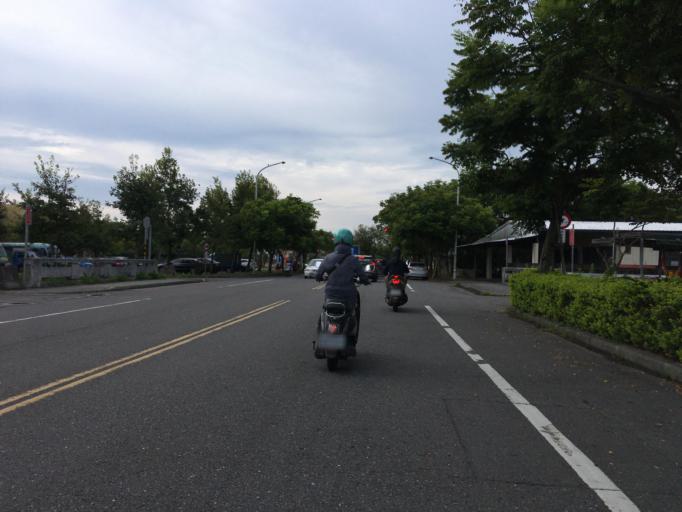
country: TW
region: Taiwan
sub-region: Yilan
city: Yilan
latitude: 24.7409
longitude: 121.7535
